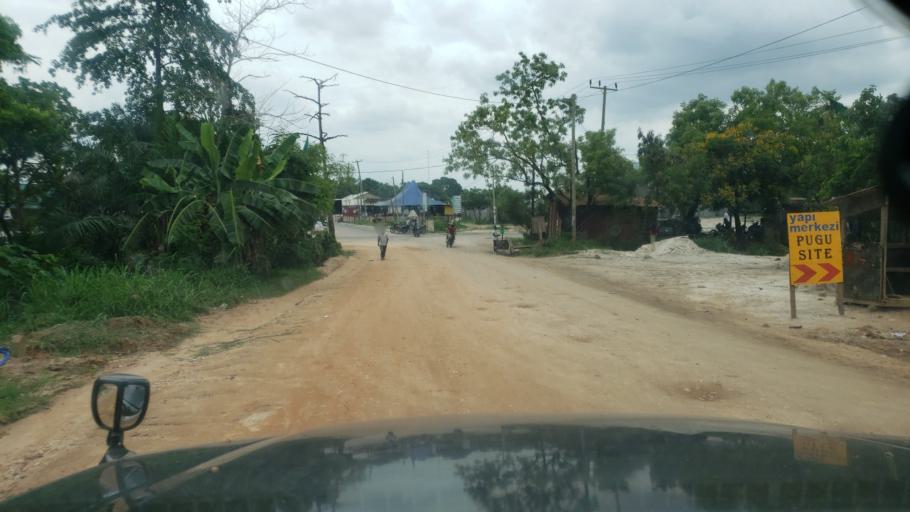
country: TZ
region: Pwani
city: Kisarawe
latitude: -6.8831
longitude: 39.1513
